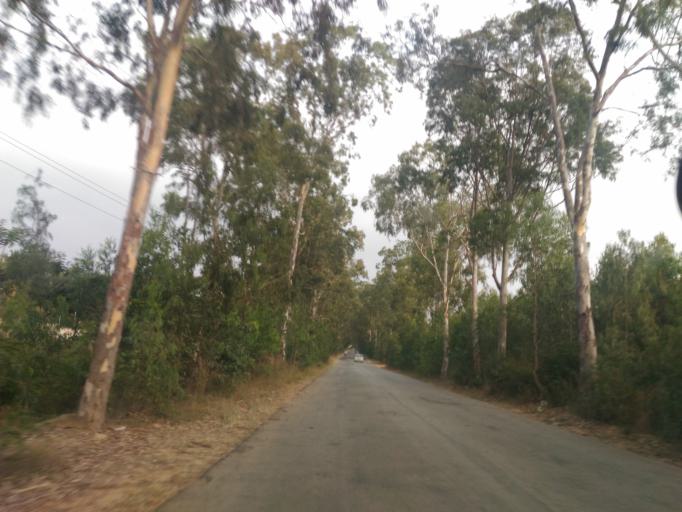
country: IN
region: Karnataka
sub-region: Chikkaballapur
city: Chik Ballapur
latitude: 13.3471
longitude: 77.6789
